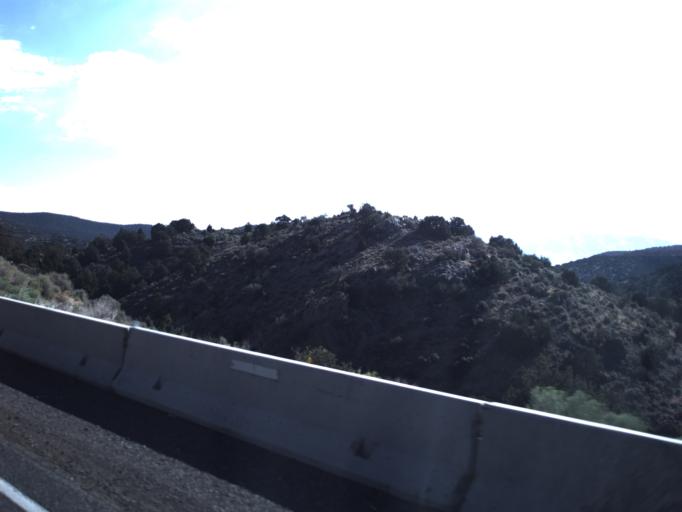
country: US
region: Utah
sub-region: Utah County
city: Genola
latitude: 39.9739
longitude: -112.0681
